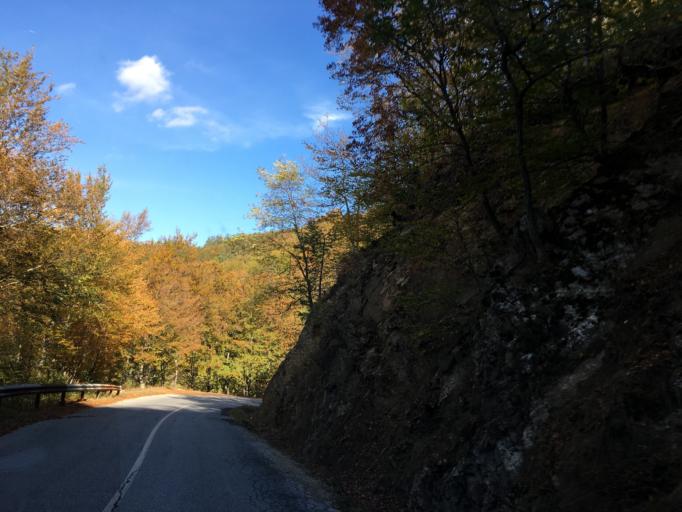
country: BG
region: Smolyan
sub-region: Obshtina Madan
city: Madan
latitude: 41.4515
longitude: 24.9777
